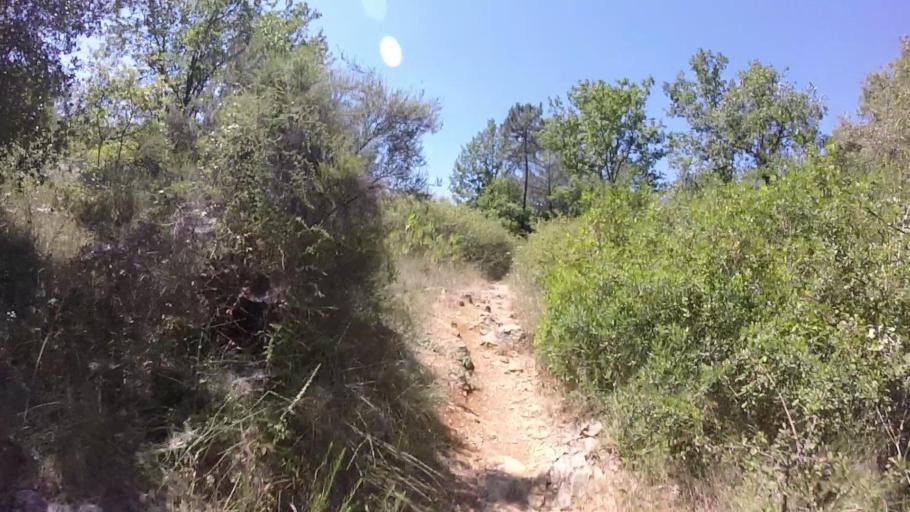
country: FR
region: Provence-Alpes-Cote d'Azur
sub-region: Departement des Alpes-Maritimes
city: Mougins
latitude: 43.6168
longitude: 7.0399
